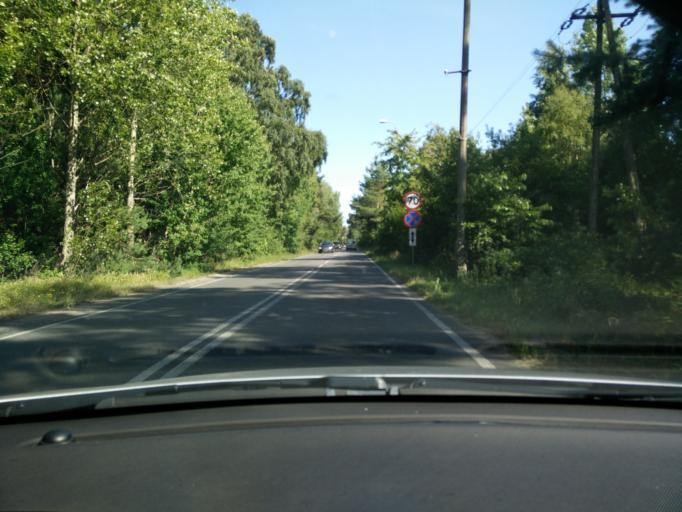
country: PL
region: Pomeranian Voivodeship
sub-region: Powiat pucki
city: Jastarnia
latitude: 54.7149
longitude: 18.6356
